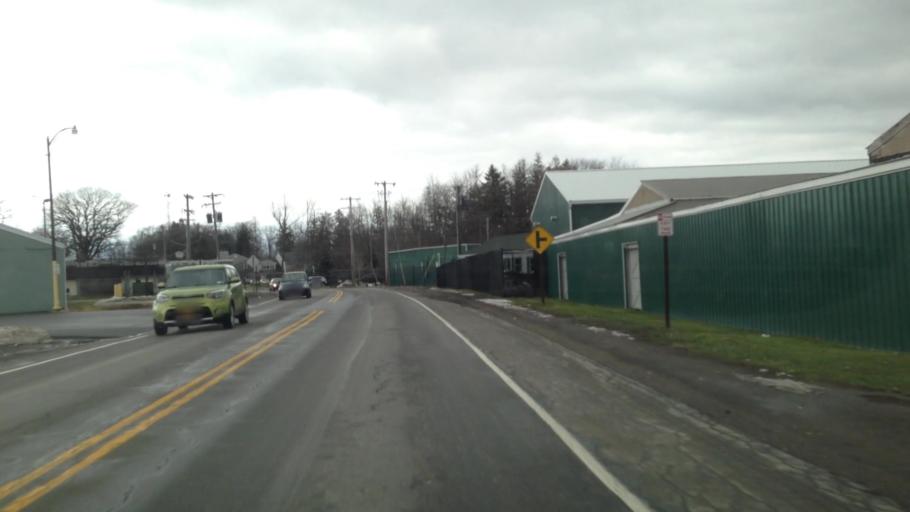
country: US
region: New York
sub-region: Genesee County
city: Batavia
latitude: 43.0108
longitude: -78.2039
